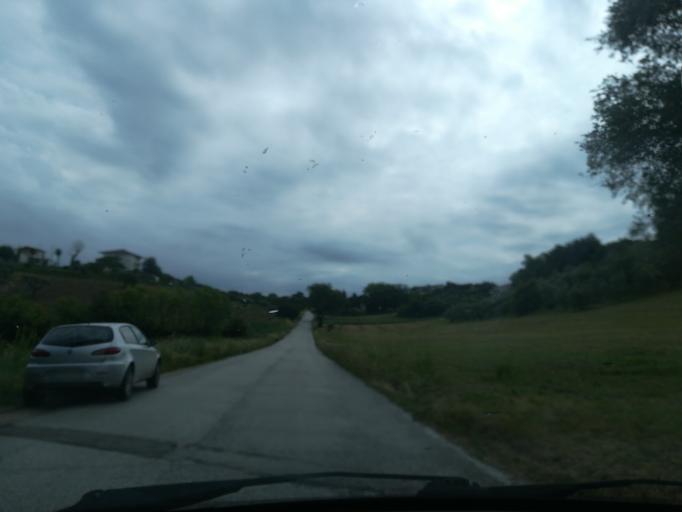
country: IT
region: The Marches
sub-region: Provincia di Macerata
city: Petriolo
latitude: 43.2254
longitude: 13.4687
